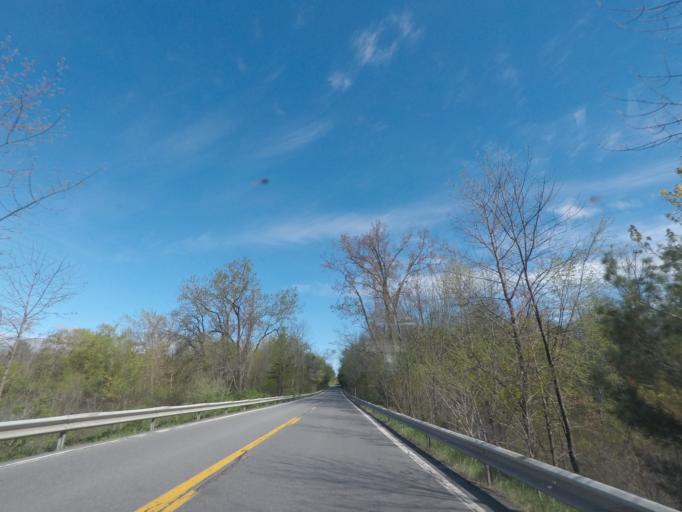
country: US
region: New York
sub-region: Albany County
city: Ravena
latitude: 42.4920
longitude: -73.9404
